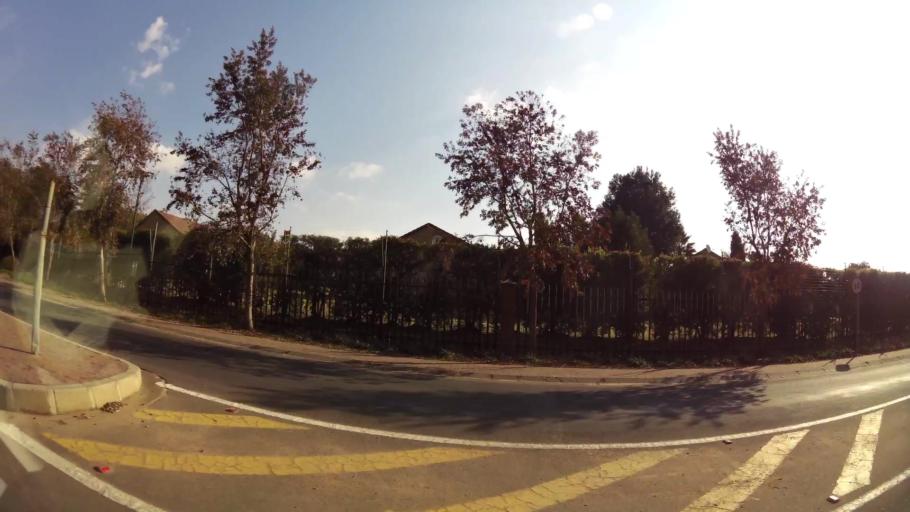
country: ZA
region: Gauteng
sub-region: City of Johannesburg Metropolitan Municipality
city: Modderfontein
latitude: -26.1025
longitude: 28.1516
